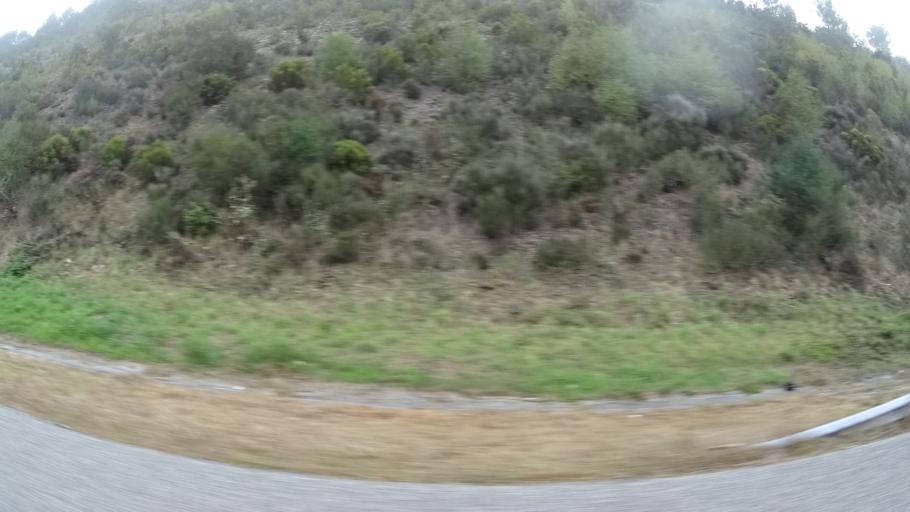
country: ES
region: Galicia
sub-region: Provincia de Lugo
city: Baralla
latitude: 42.9129
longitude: -7.1967
